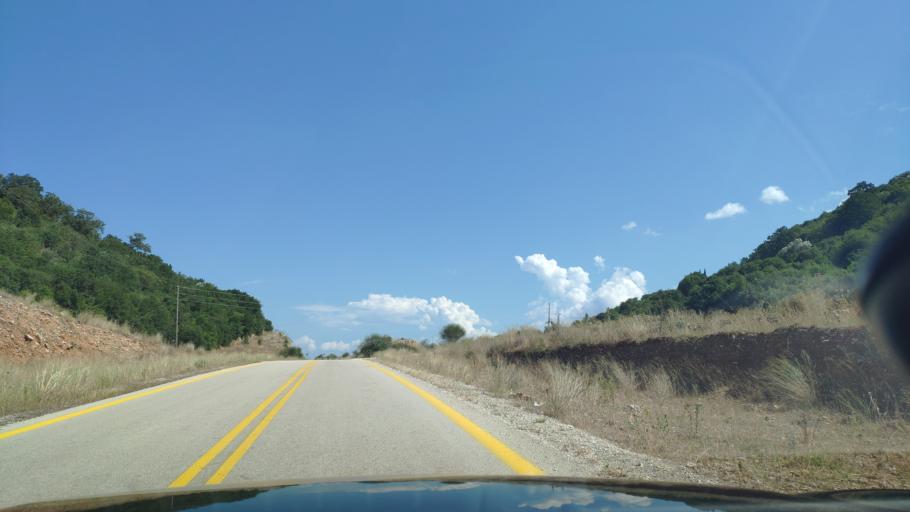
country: GR
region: West Greece
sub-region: Nomos Aitolias kai Akarnanias
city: Katouna
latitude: 38.8564
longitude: 21.0867
